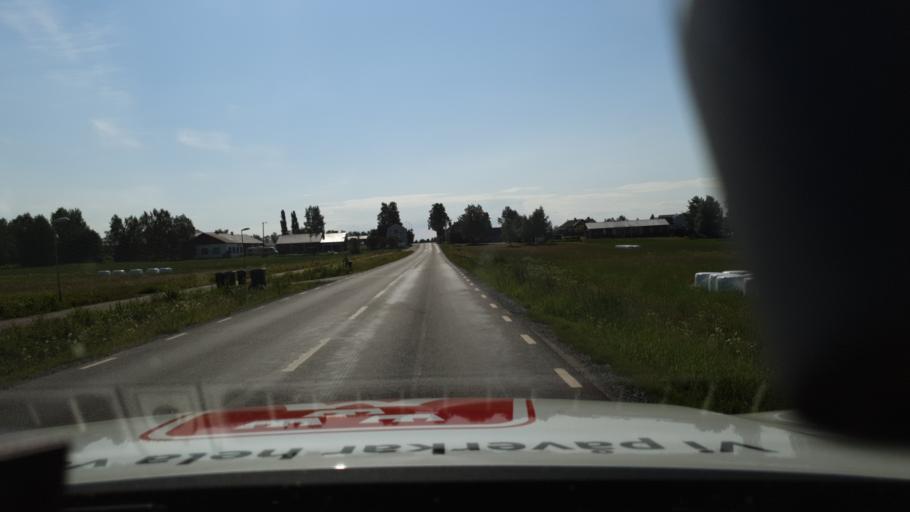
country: SE
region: Norrbotten
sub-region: Lulea Kommun
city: Sodra Sunderbyn
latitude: 65.8133
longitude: 22.0107
